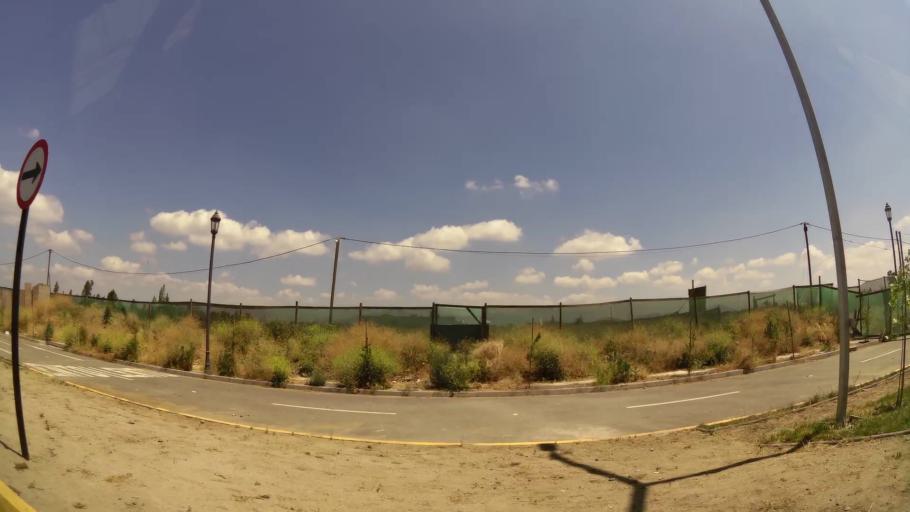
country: CL
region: Santiago Metropolitan
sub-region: Provincia de Talagante
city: Penaflor
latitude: -33.5721
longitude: -70.7954
